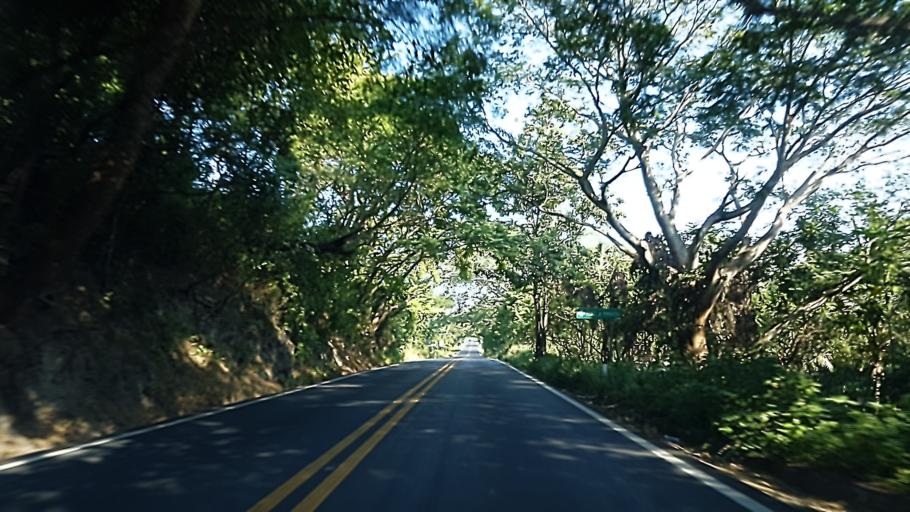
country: MX
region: Nayarit
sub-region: Compostela
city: Colonia Paraiso Escondido
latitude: 21.0067
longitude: -105.2718
